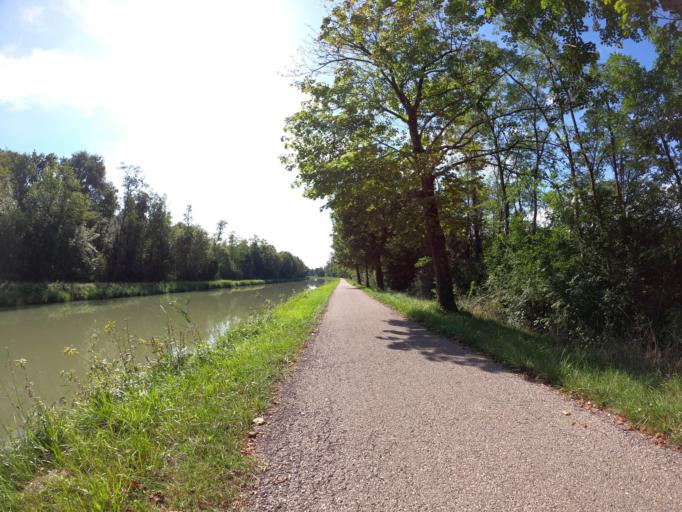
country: FR
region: Midi-Pyrenees
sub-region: Departement du Tarn-et-Garonne
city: Montech
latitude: 43.9418
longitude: 1.2532
